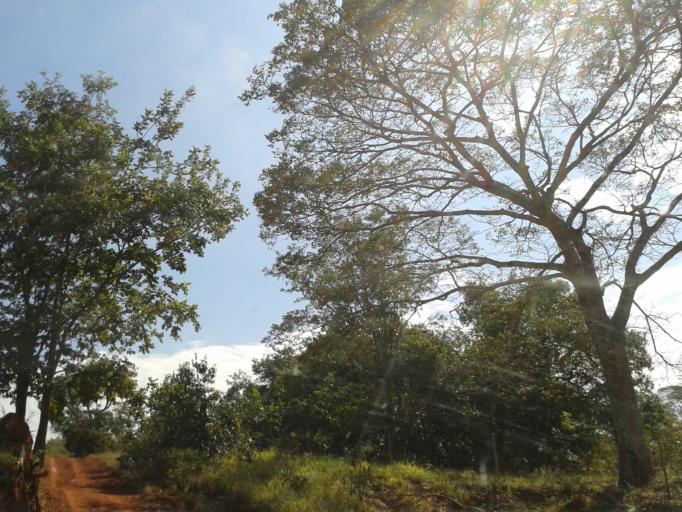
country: BR
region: Minas Gerais
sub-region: Campina Verde
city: Campina Verde
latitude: -19.3857
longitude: -49.6625
